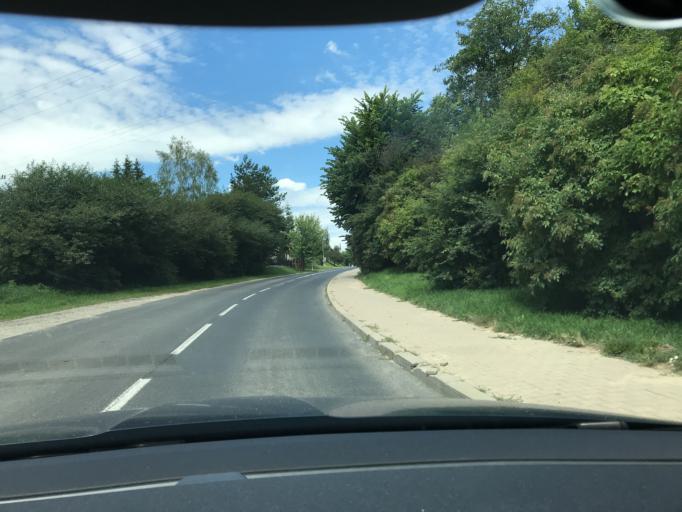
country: PL
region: Lublin Voivodeship
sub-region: Powiat zamojski
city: Szczebrzeszyn
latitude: 50.6993
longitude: 22.9673
